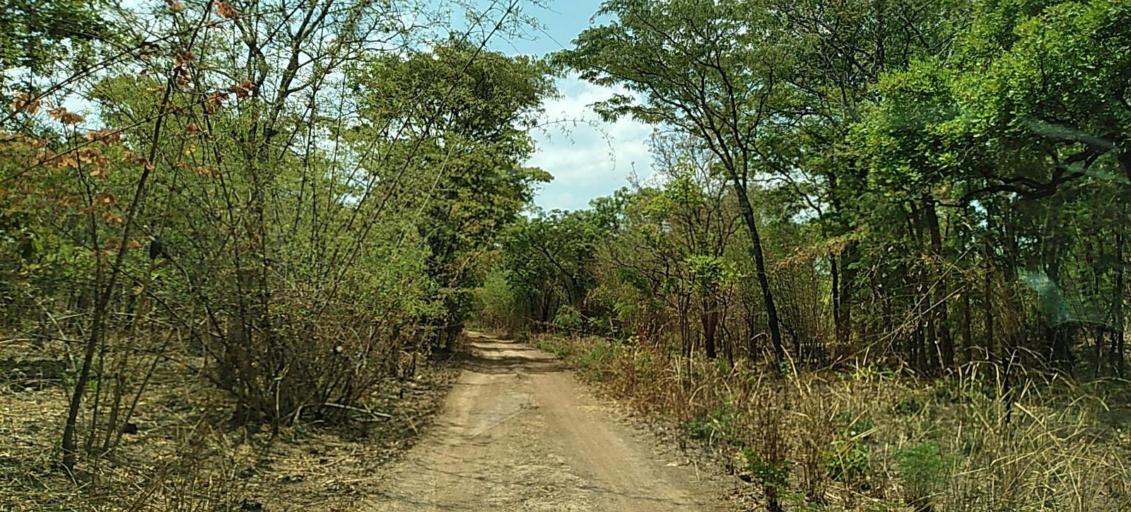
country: ZM
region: Copperbelt
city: Chililabombwe
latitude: -12.4688
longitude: 27.6498
